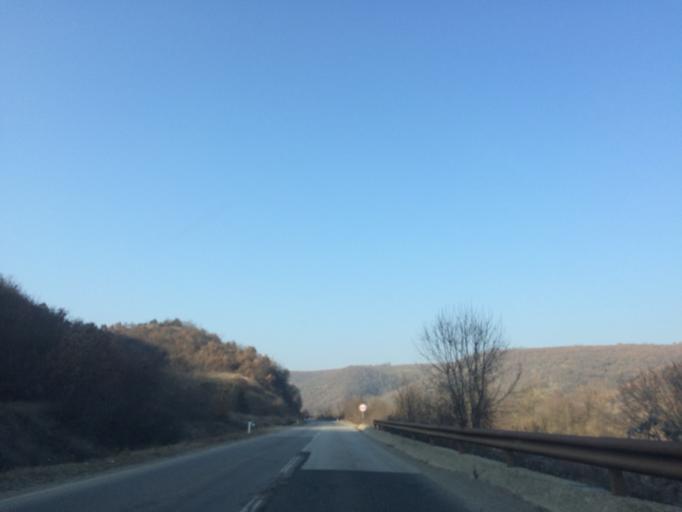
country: XK
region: Pec
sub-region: Komuna e Pejes
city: Kosuriq
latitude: 42.5064
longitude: 20.5342
